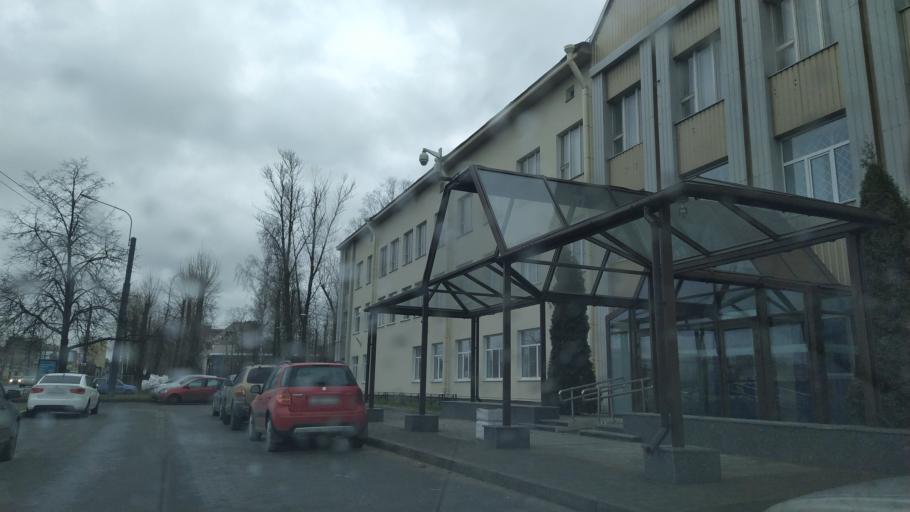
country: RU
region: Leningrad
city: Svetlanovskiy
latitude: 60.0067
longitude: 30.3370
